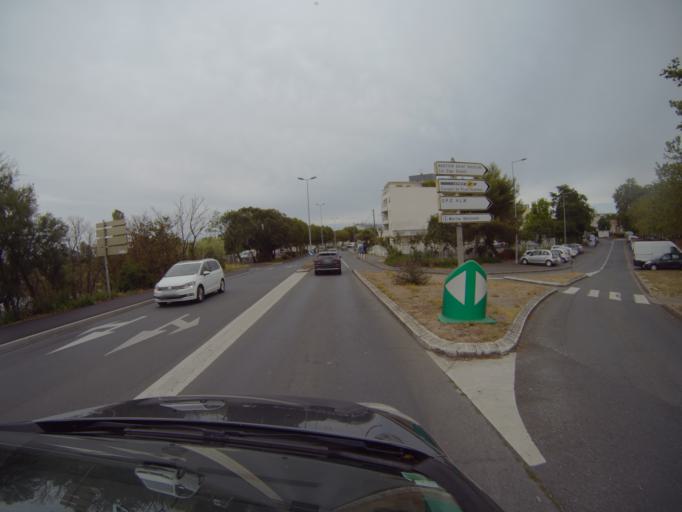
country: FR
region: Poitou-Charentes
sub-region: Departement de la Charente-Maritime
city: La Rochelle
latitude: 46.1558
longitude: -1.1430
